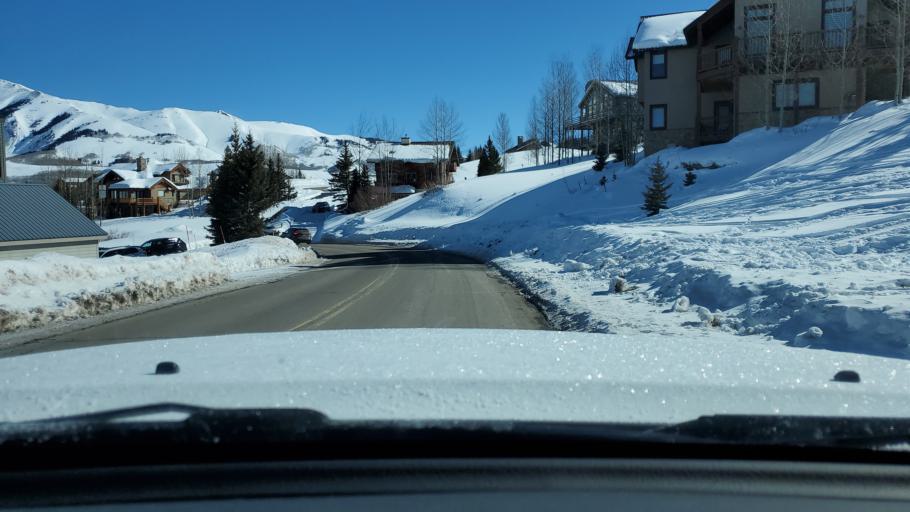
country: US
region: Colorado
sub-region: Gunnison County
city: Crested Butte
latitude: 38.9117
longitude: -106.9624
